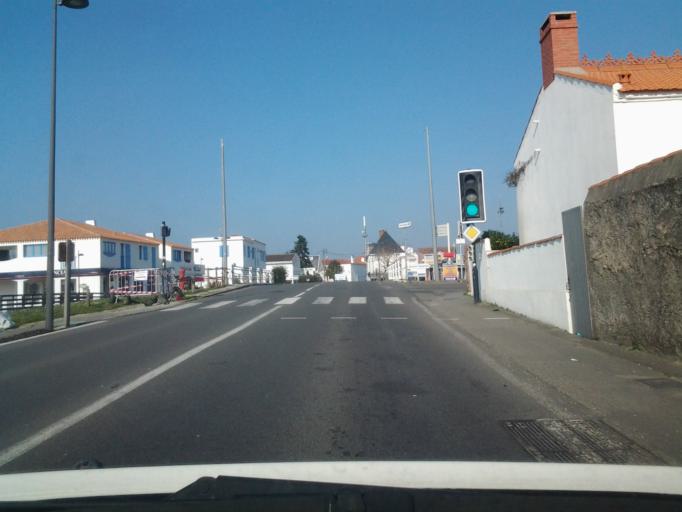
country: FR
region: Pays de la Loire
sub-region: Departement de la Vendee
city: La Gueriniere
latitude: 46.9993
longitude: -2.2480
